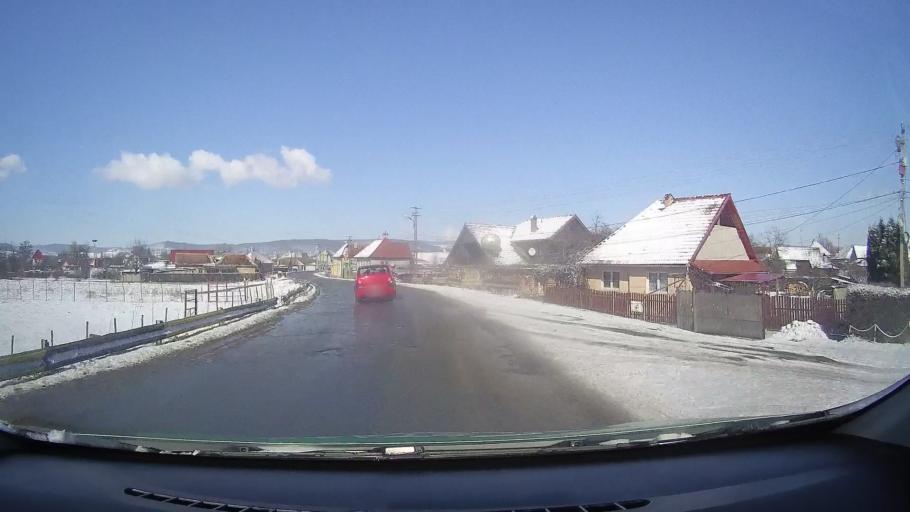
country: RO
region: Sibiu
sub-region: Comuna Avrig
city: Avrig
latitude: 45.7200
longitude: 24.3737
